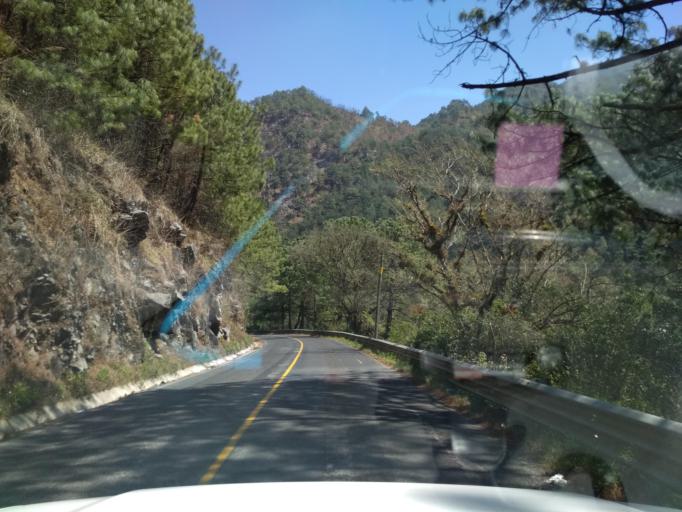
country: MX
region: Veracruz
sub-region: Tlilapan
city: Tonalixco
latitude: 18.7695
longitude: -97.0806
